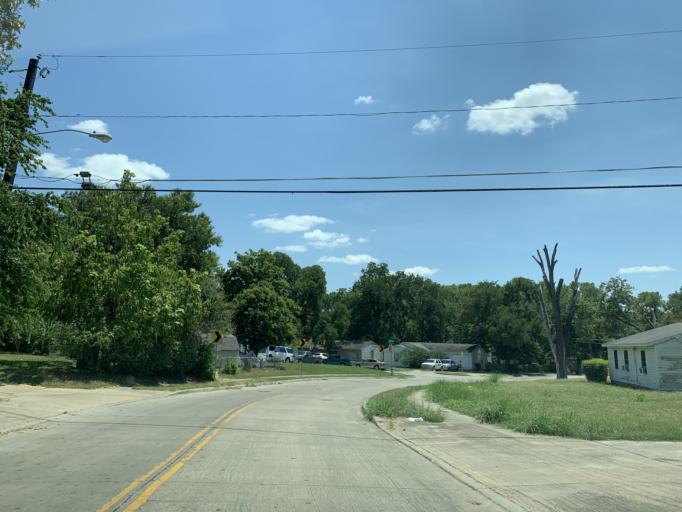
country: US
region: Texas
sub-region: Dallas County
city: Hutchins
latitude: 32.6859
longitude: -96.7771
